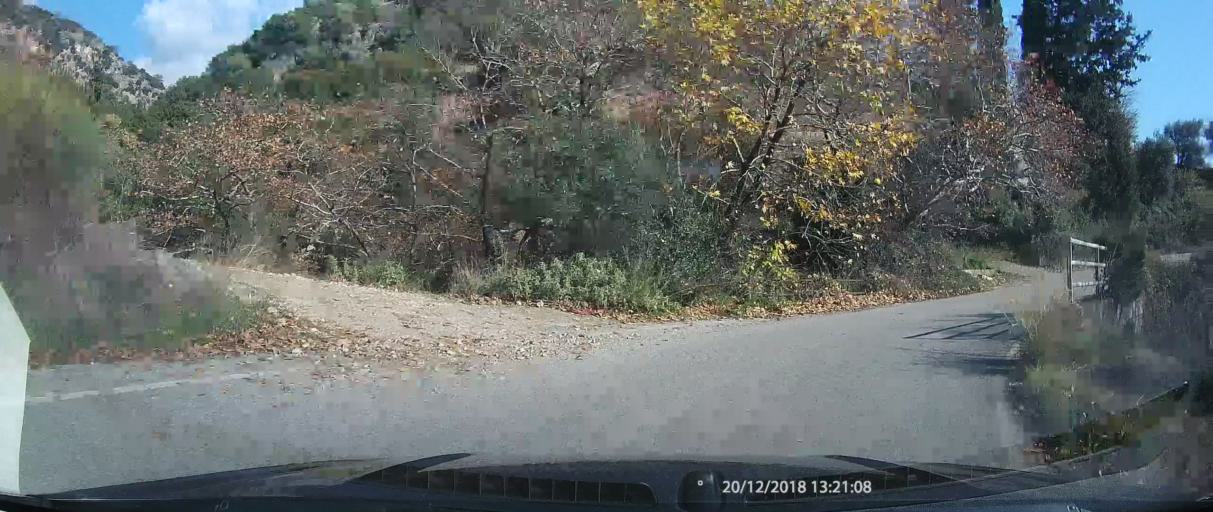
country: GR
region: West Greece
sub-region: Nomos Aitolias kai Akarnanias
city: Paravola
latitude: 38.6187
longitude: 21.5527
